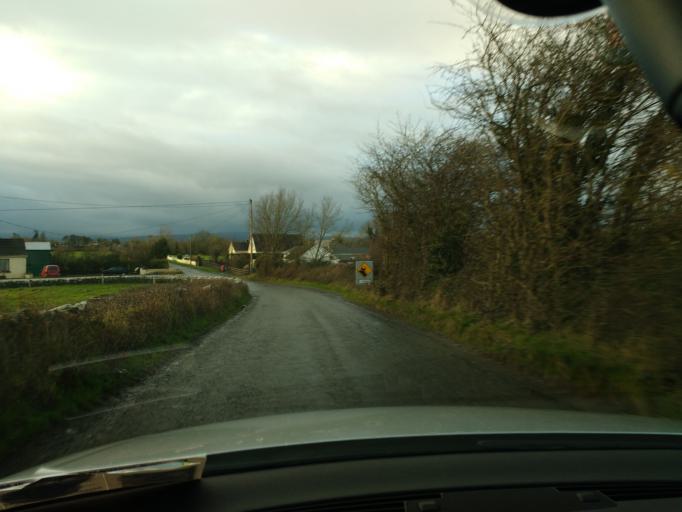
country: IE
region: Munster
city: Thurles
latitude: 52.6336
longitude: -7.8109
